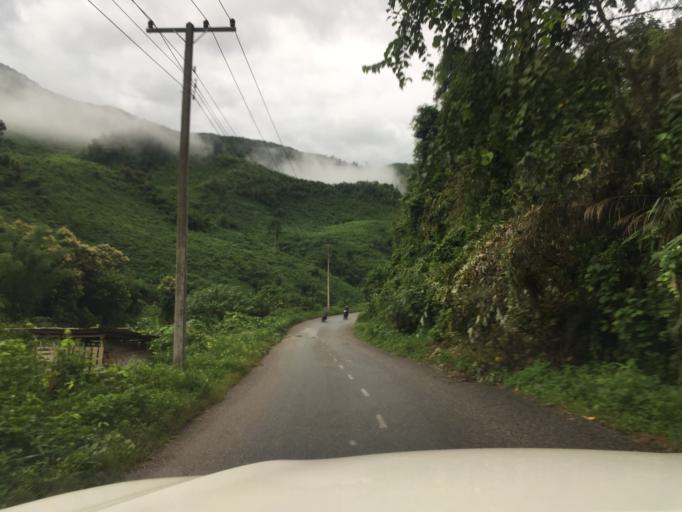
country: LA
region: Oudomxai
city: Muang La
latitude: 21.0316
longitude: 102.2367
